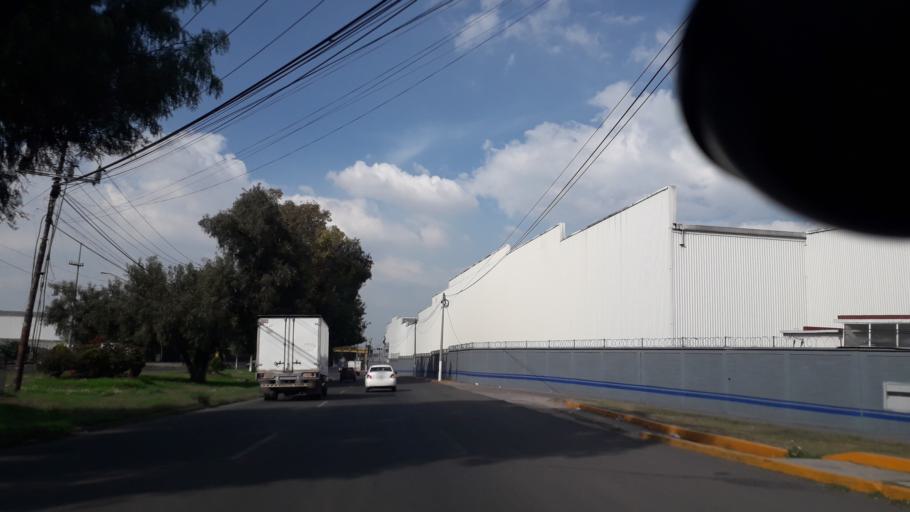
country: MX
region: Mexico
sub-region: Tultitlan
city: Buenavista
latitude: 19.6185
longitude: -99.1858
